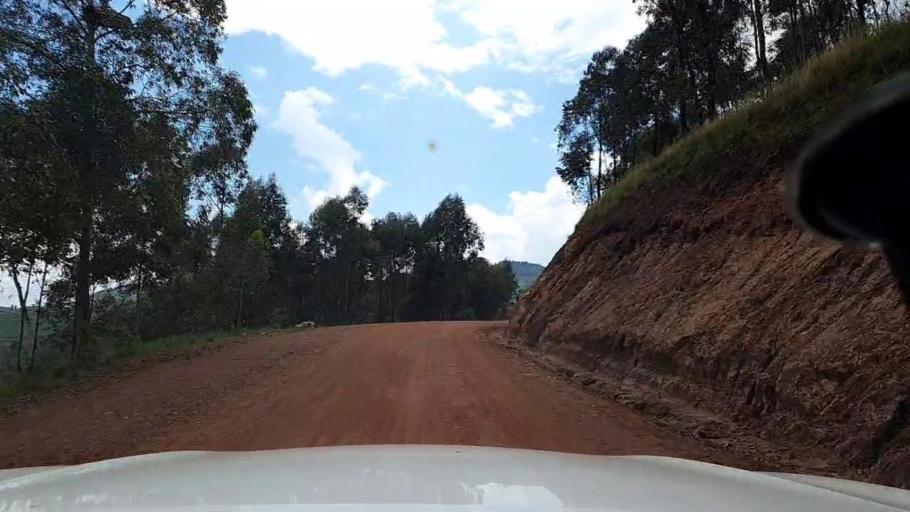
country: RW
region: Kigali
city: Kigali
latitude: -1.7610
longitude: 29.8423
